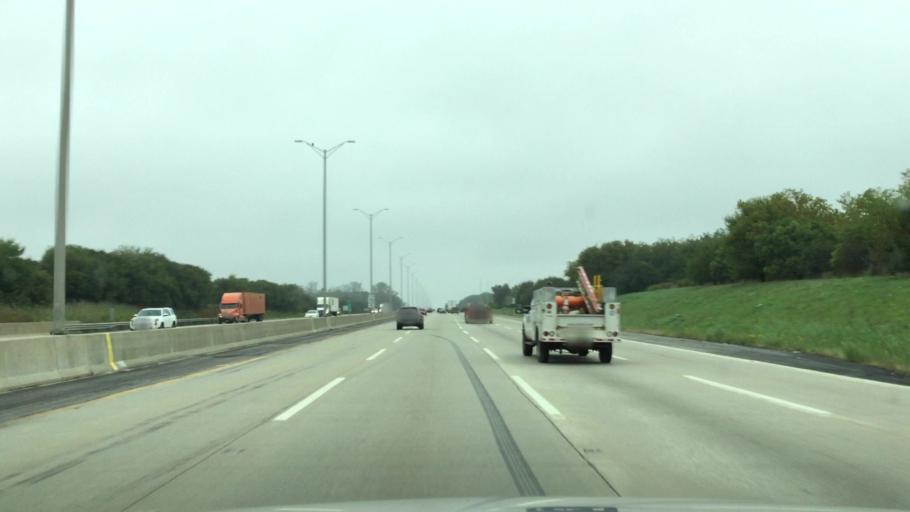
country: US
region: Illinois
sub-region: Lake County
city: Grandwood Park
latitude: 42.3937
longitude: -87.9489
